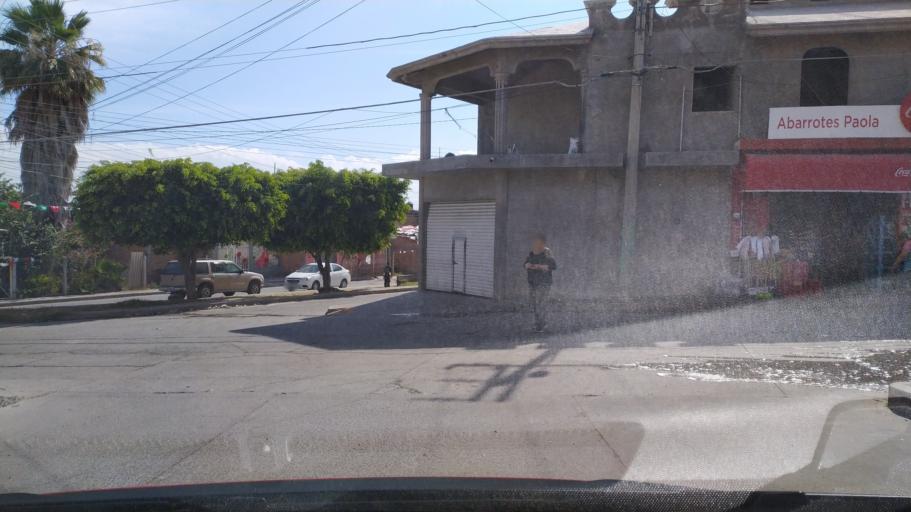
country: MX
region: Guanajuato
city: Ciudad Manuel Doblado
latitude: 20.7331
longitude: -101.9551
